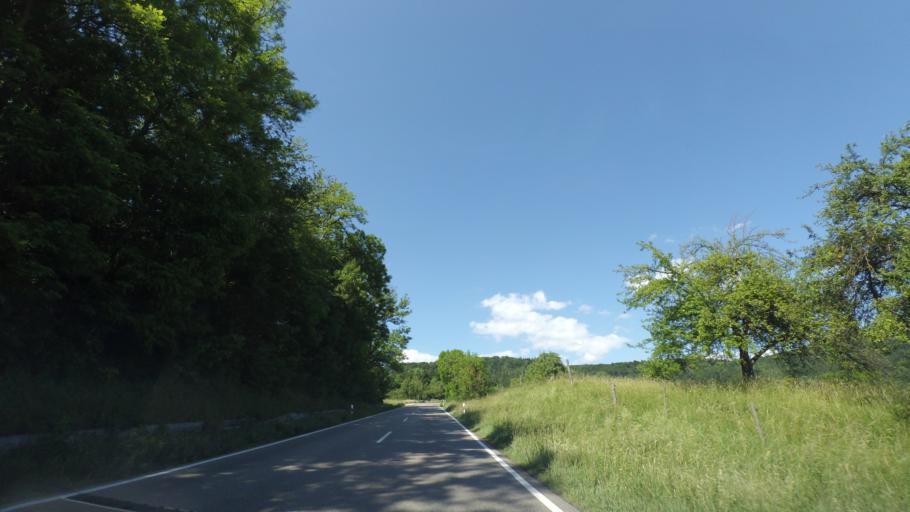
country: DE
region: Baden-Wuerttemberg
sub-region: Regierungsbezirk Stuttgart
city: Gaildorf
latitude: 49.0091
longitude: 9.7771
